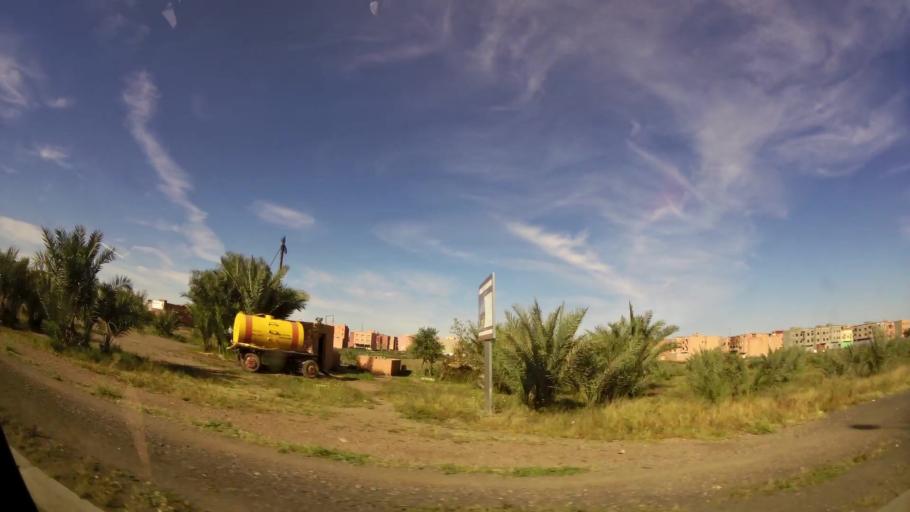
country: MA
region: Marrakech-Tensift-Al Haouz
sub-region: Marrakech
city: Marrakesh
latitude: 31.6764
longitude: -8.0455
